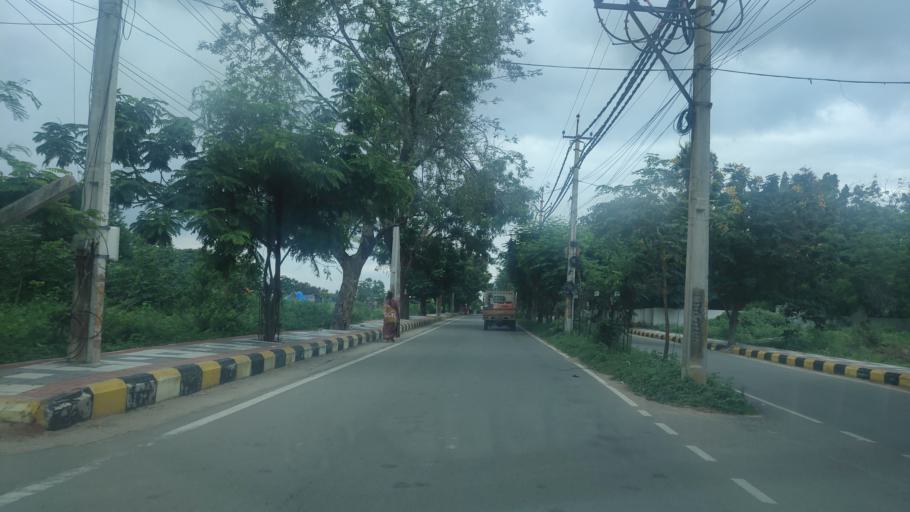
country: IN
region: Telangana
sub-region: Medak
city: Serilingampalle
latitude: 17.5037
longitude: 78.3521
